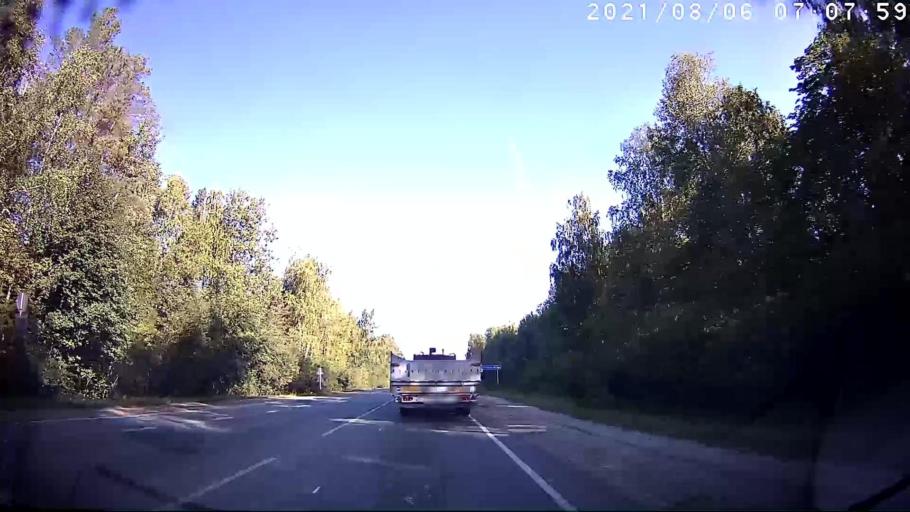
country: RU
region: Mariy-El
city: Yoshkar-Ola
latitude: 56.5667
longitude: 47.9752
